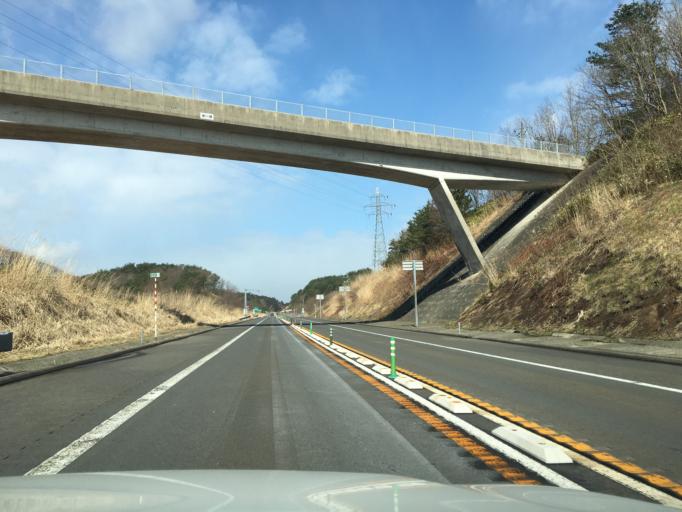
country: JP
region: Akita
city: Akita
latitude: 39.7581
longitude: 140.1340
